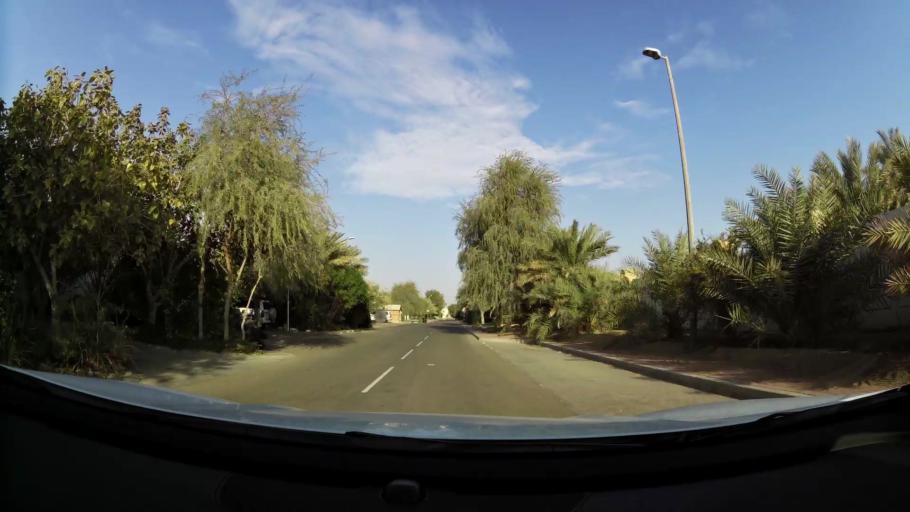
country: AE
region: Abu Dhabi
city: Al Ain
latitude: 24.0821
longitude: 55.8438
